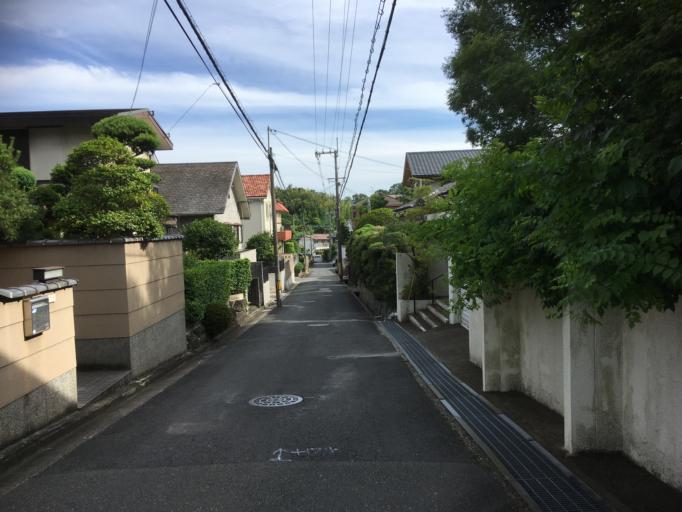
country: JP
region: Nara
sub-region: Ikoma-shi
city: Ikoma
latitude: 34.6990
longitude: 135.7389
